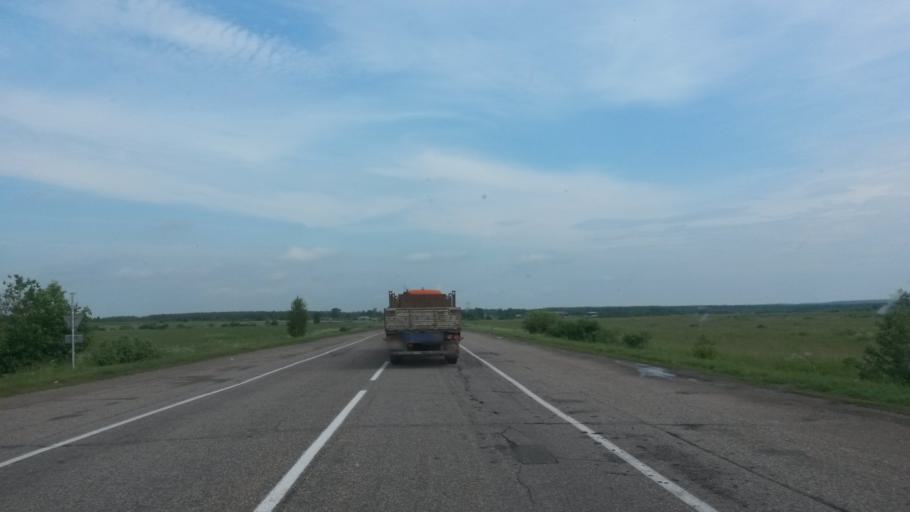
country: RU
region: Jaroslavl
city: Gavrilov-Yam
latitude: 57.3083
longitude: 39.8852
